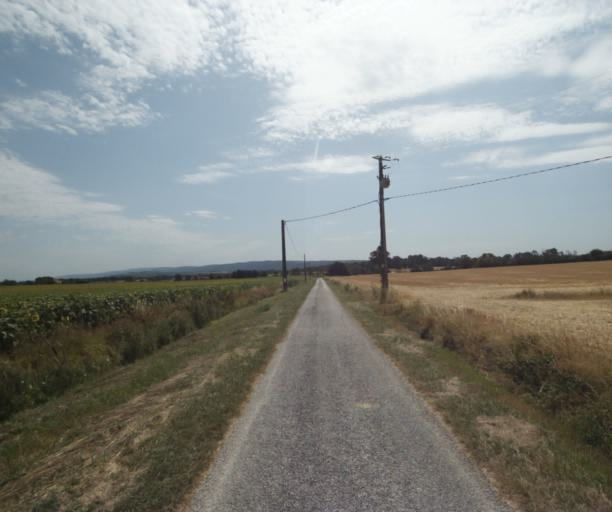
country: FR
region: Midi-Pyrenees
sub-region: Departement de la Haute-Garonne
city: Saint-Felix-Lauragais
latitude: 43.4352
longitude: 1.9069
